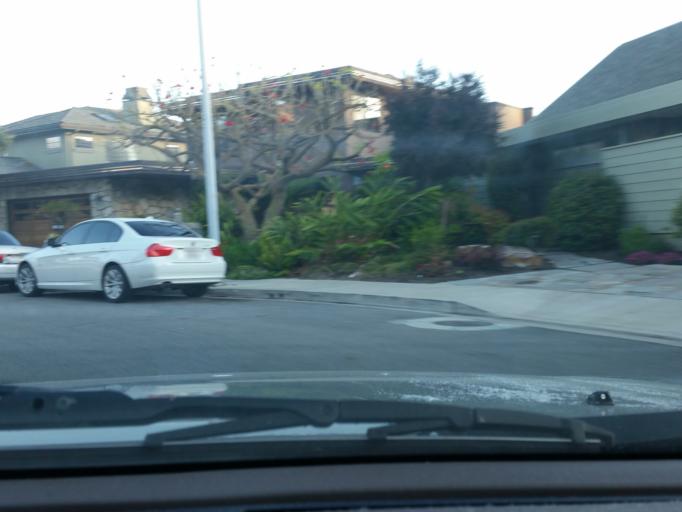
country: US
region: California
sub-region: San Luis Obispo County
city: Avila Beach
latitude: 35.1627
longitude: -120.6884
